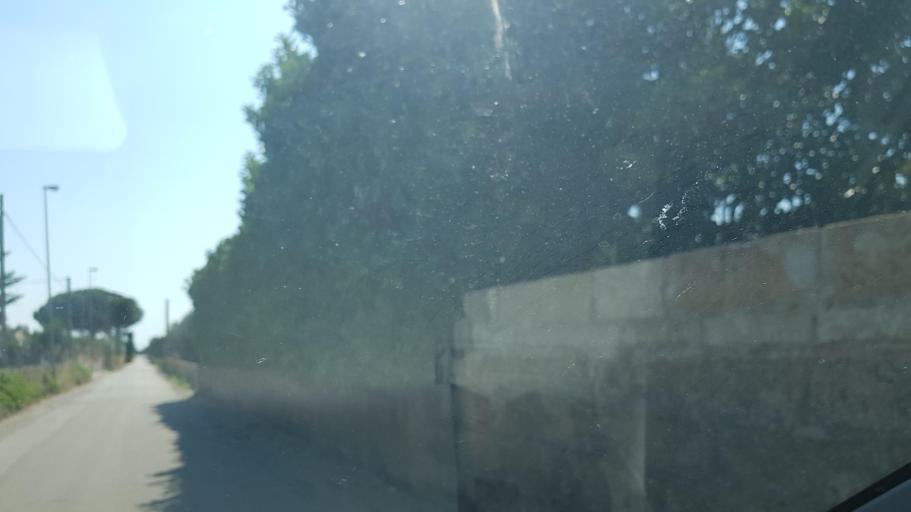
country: IT
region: Apulia
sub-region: Provincia di Lecce
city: Torre San Giovanni
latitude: 39.8897
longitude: 18.1246
